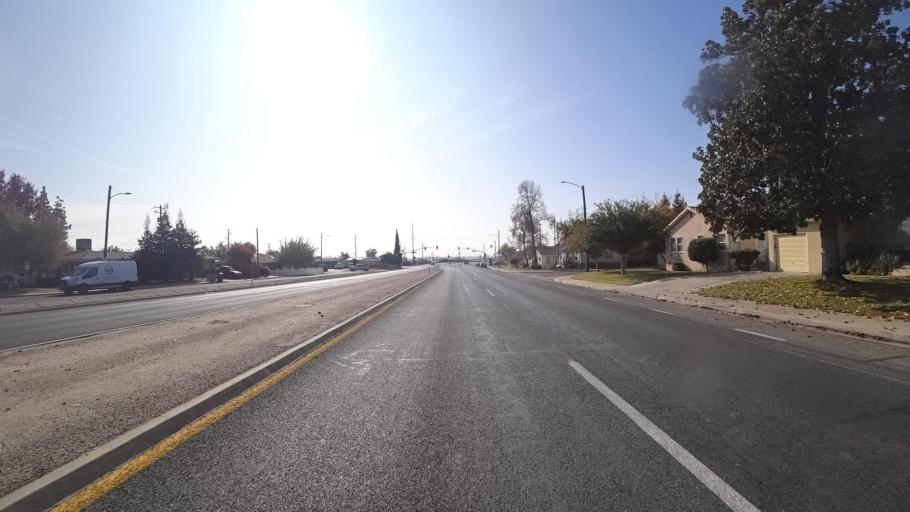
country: US
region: California
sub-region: Kern County
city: Oildale
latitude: 35.4283
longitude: -119.0125
